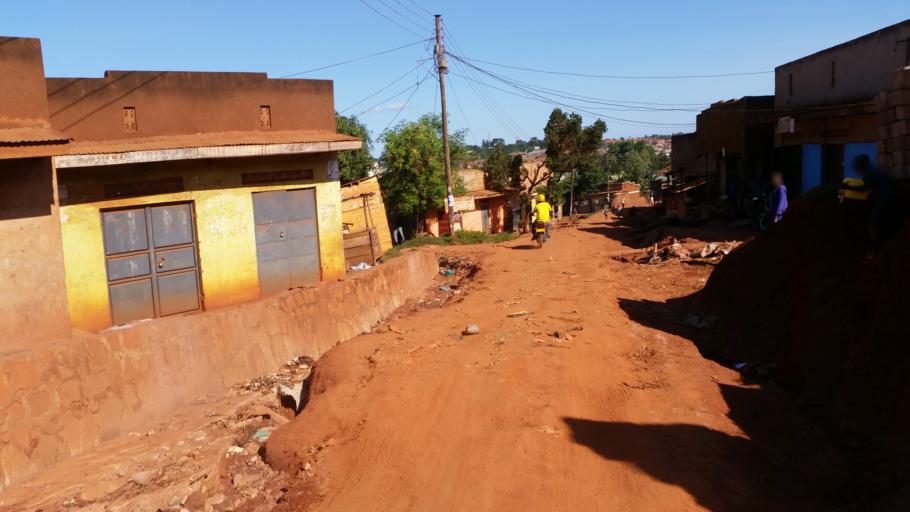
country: UG
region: Central Region
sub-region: Wakiso District
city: Kireka
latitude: 0.3323
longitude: 32.6527
